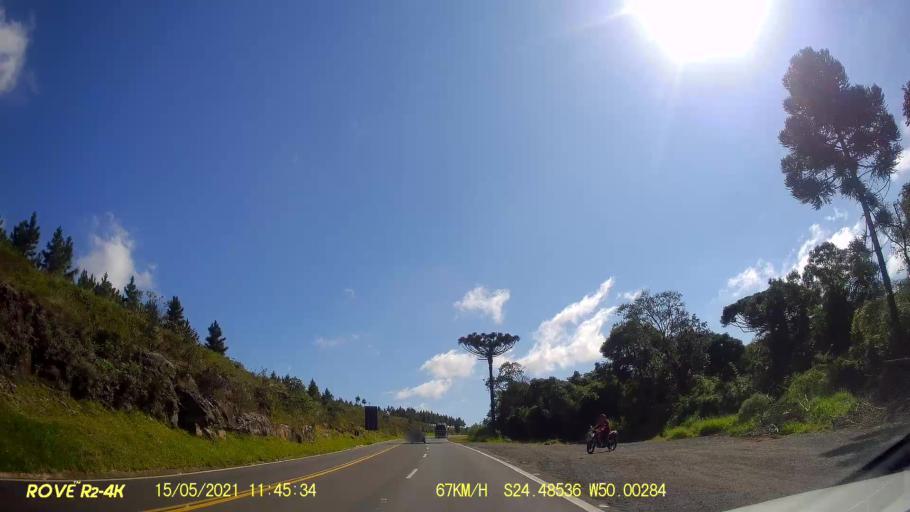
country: BR
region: Parana
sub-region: Pirai Do Sul
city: Pirai do Sul
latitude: -24.4854
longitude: -50.0028
